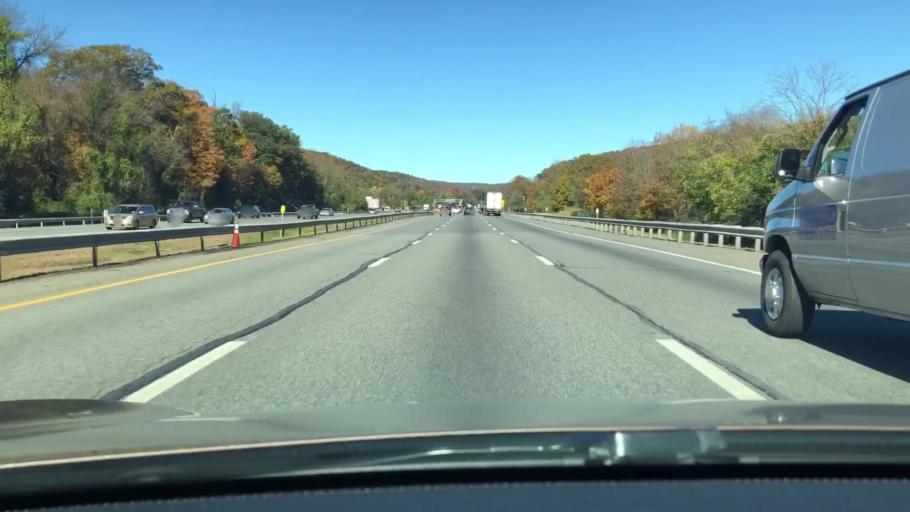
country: US
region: New York
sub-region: Rockland County
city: Sloatsburg
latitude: 41.1883
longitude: -74.1811
